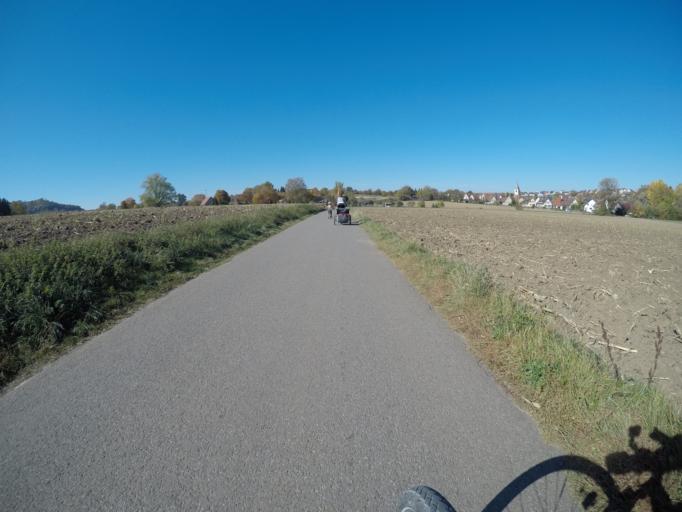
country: DE
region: Baden-Wuerttemberg
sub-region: Tuebingen Region
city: Rottenburg
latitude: 48.5307
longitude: 8.9506
